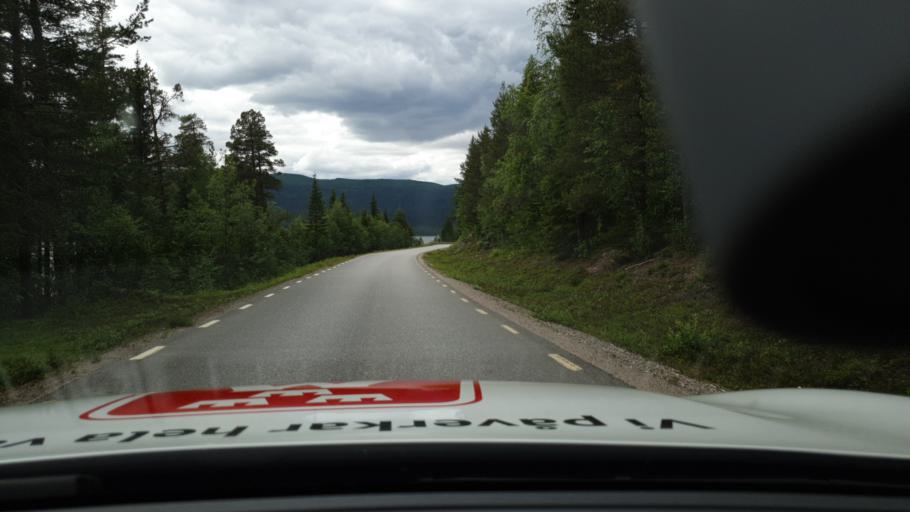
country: SE
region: Norrbotten
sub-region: Arjeplogs Kommun
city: Arjeplog
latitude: 66.8974
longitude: 17.8498
